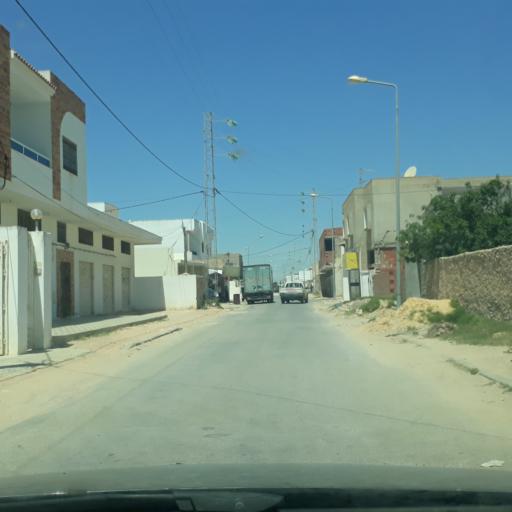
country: TN
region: Safaqis
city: Al Qarmadah
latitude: 34.8162
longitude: 10.7576
